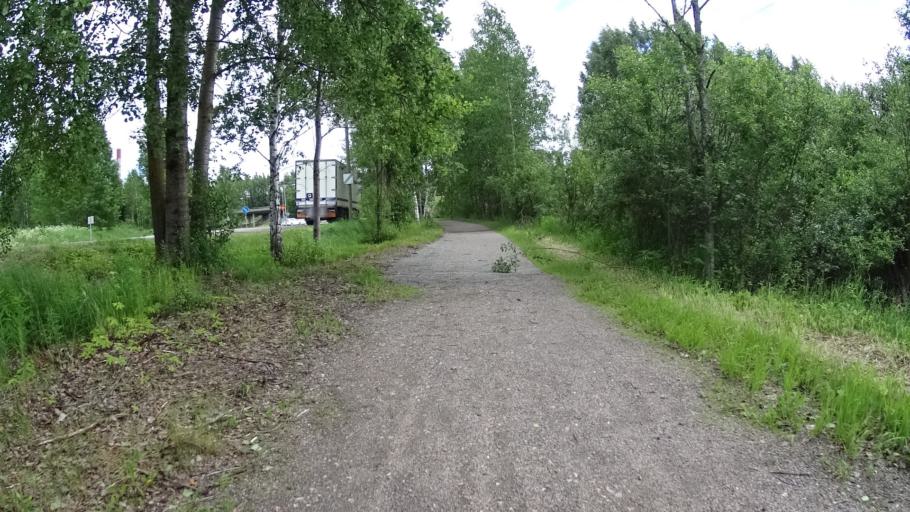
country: FI
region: Uusimaa
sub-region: Helsinki
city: Kilo
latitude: 60.2859
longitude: 24.8258
